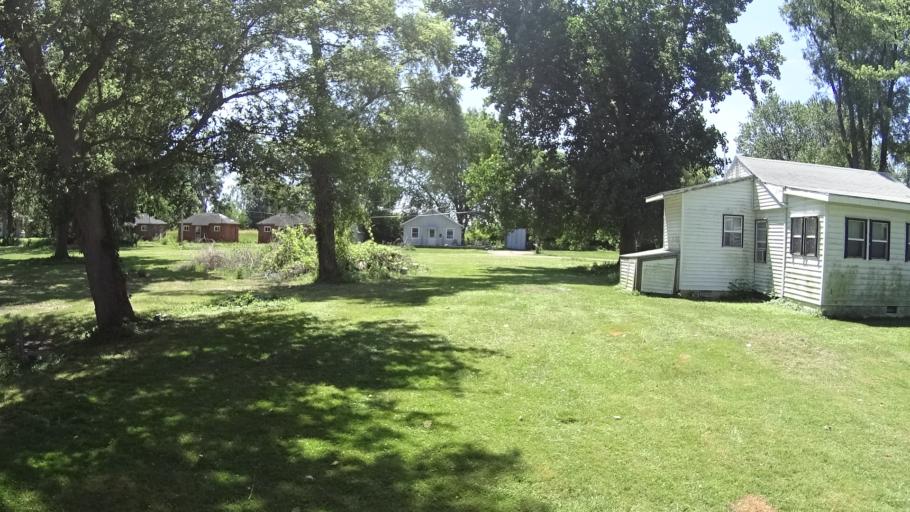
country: US
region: Ohio
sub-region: Ottawa County
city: Port Clinton
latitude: 41.4499
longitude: -82.8397
